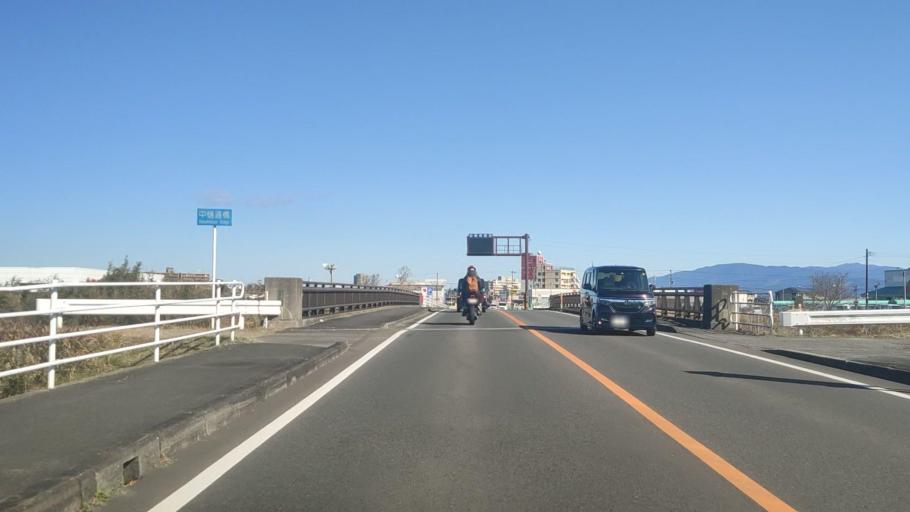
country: JP
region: Miyazaki
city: Miyakonojo
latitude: 31.7107
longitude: 131.0559
